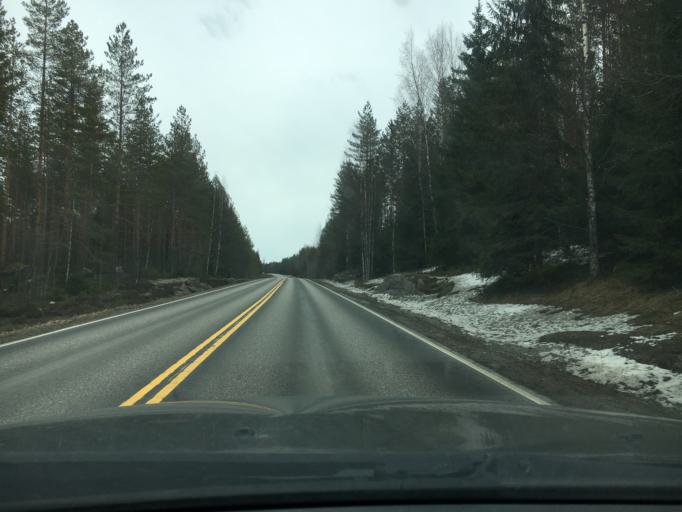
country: FI
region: Central Finland
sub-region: AEaenekoski
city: Sumiainen
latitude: 62.5539
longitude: 26.0108
